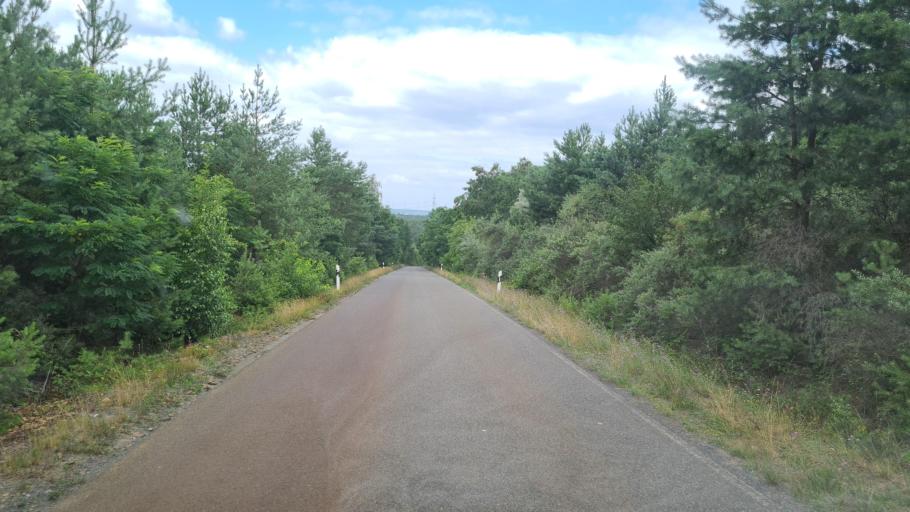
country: DE
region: Brandenburg
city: Altdobern
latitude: 51.6590
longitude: 14.1065
